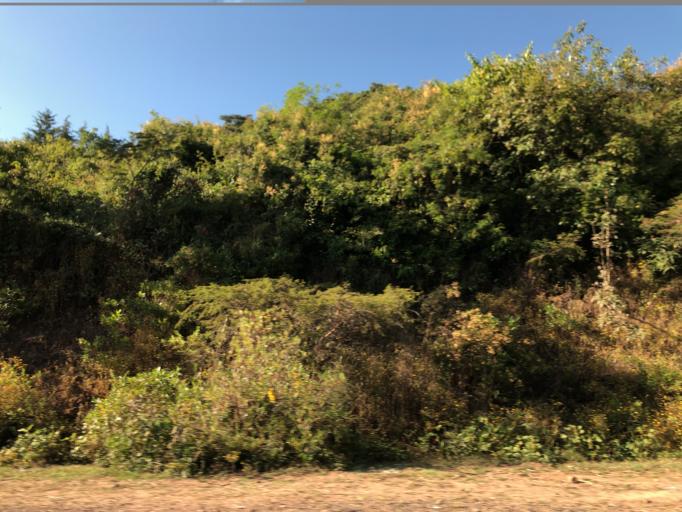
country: ET
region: Amhara
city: Debre Tabor
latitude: 11.9257
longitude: 37.9455
